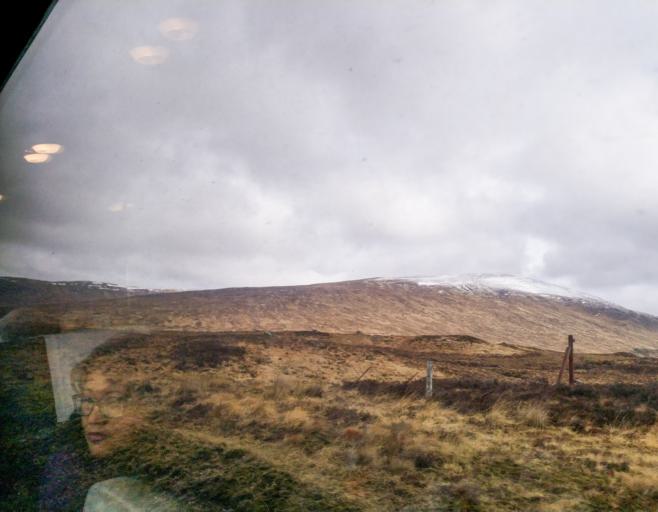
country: GB
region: Scotland
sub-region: Highland
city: Spean Bridge
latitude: 56.7582
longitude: -4.6876
